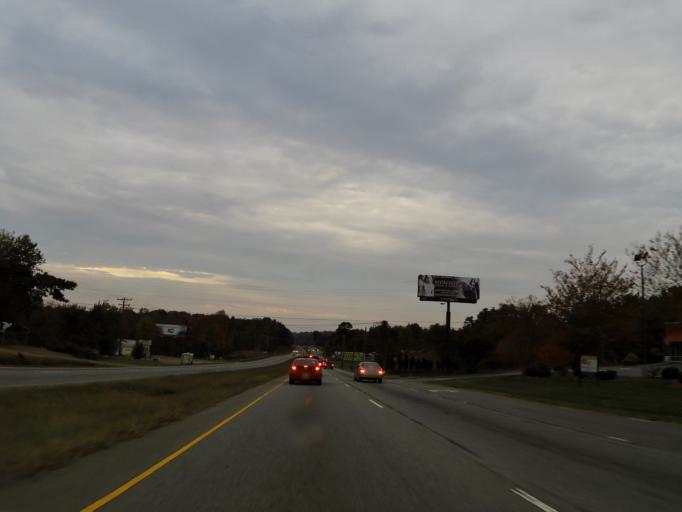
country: US
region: North Carolina
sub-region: Caldwell County
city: Northlakes
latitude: 35.7660
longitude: -81.3854
